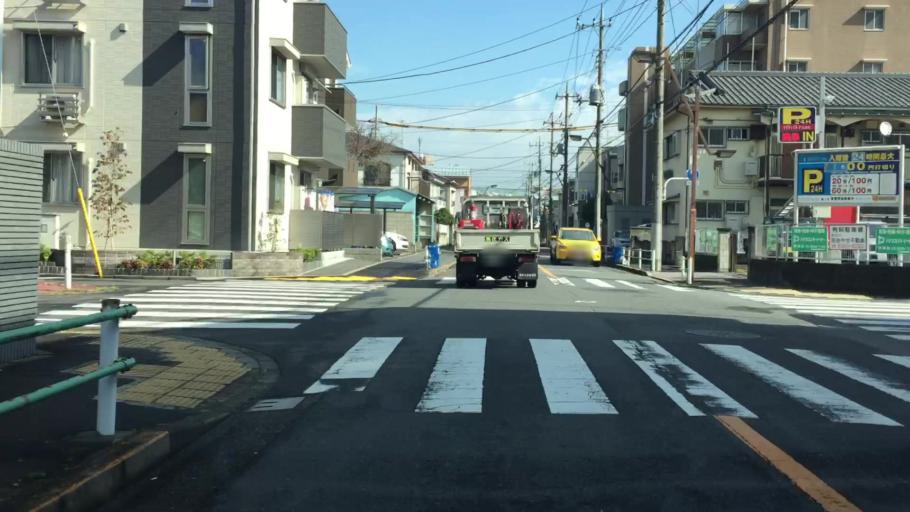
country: JP
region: Saitama
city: Yashio-shi
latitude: 35.7613
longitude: 139.8377
